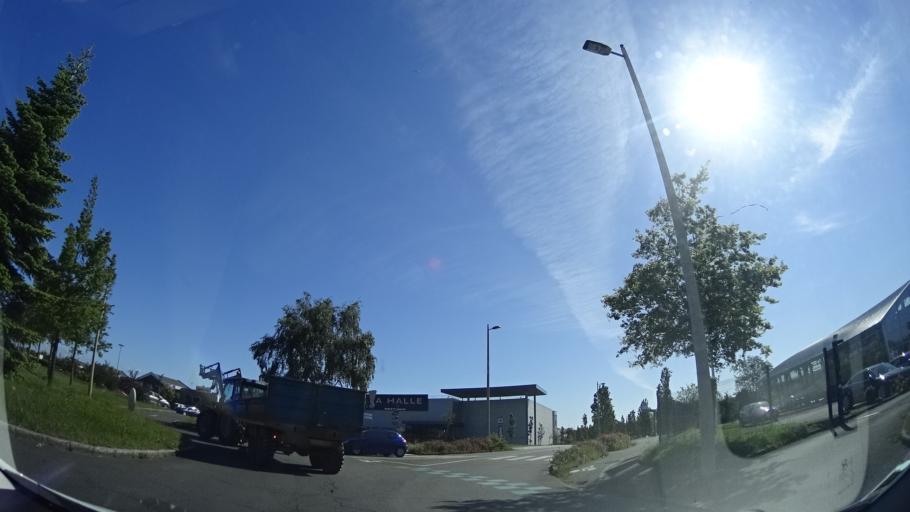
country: FR
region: Brittany
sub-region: Departement d'Ille-et-Vilaine
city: Saint-Jouan-des-Guerets
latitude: 48.6229
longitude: -1.9867
